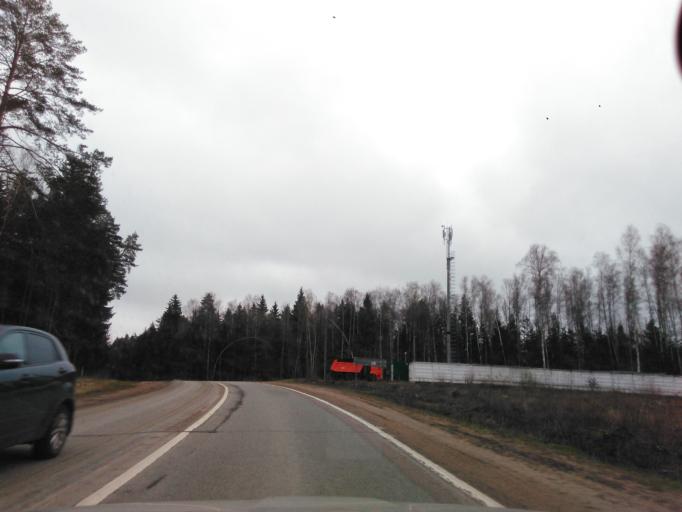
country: RU
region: Moskovskaya
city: Snegiri
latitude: 55.8409
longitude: 36.9701
